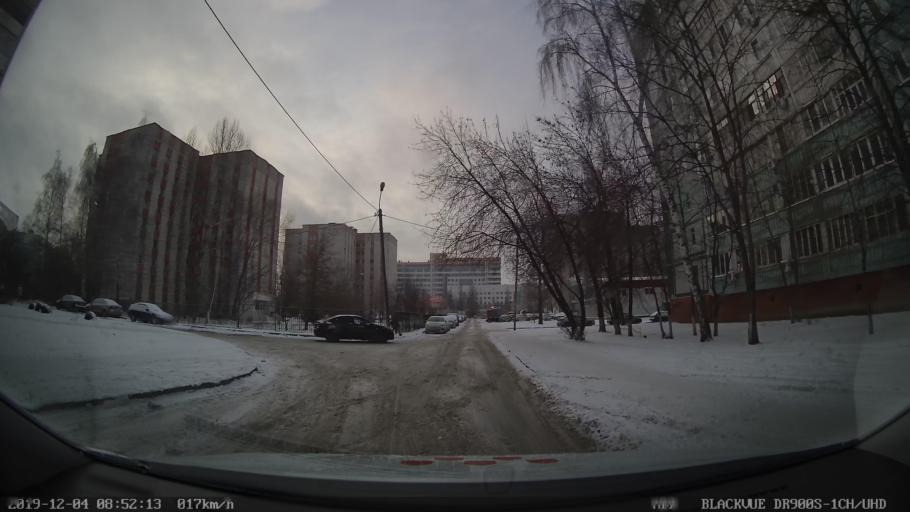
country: RU
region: Tatarstan
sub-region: Gorod Kazan'
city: Kazan
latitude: 55.8378
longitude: 49.1385
